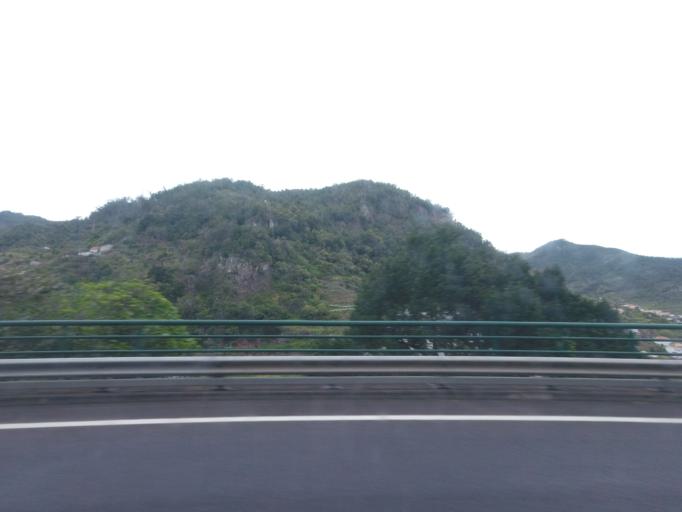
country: PT
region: Madeira
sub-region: Machico
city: Machico
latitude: 32.7329
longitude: -16.7867
